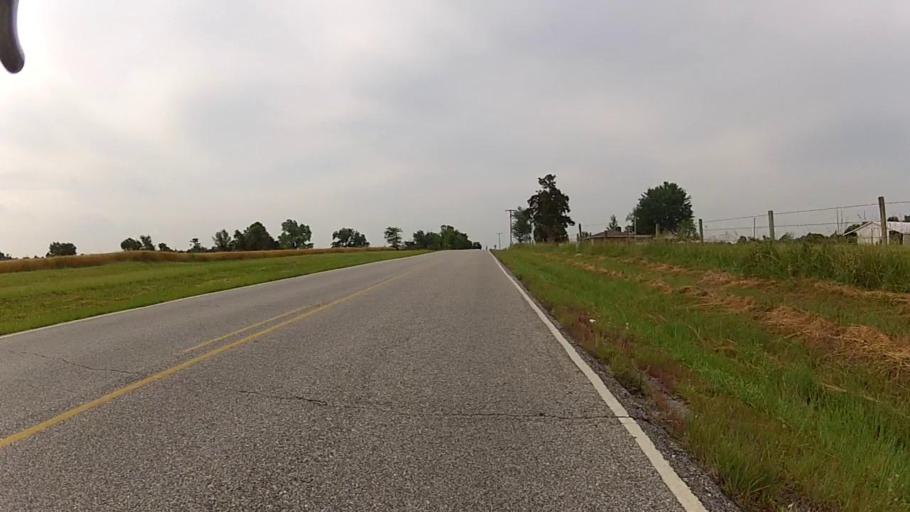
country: US
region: Kansas
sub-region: Cherokee County
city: Baxter Springs
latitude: 37.0807
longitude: -94.7225
